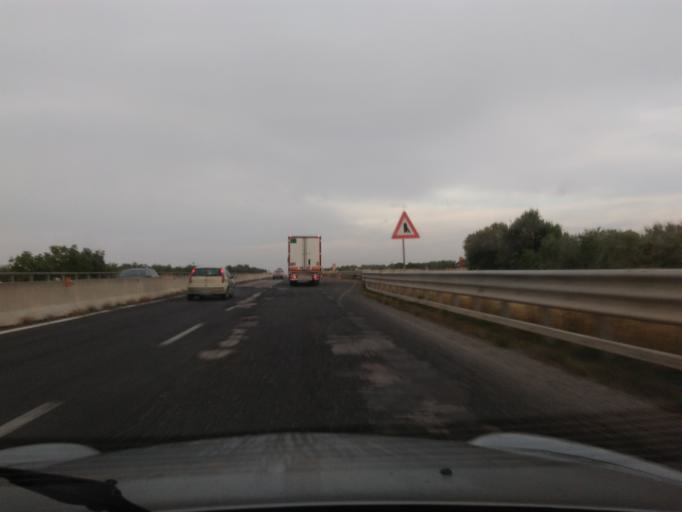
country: IT
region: Apulia
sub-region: Provincia di Bari
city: Molfetta
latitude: 41.1856
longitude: 16.6317
